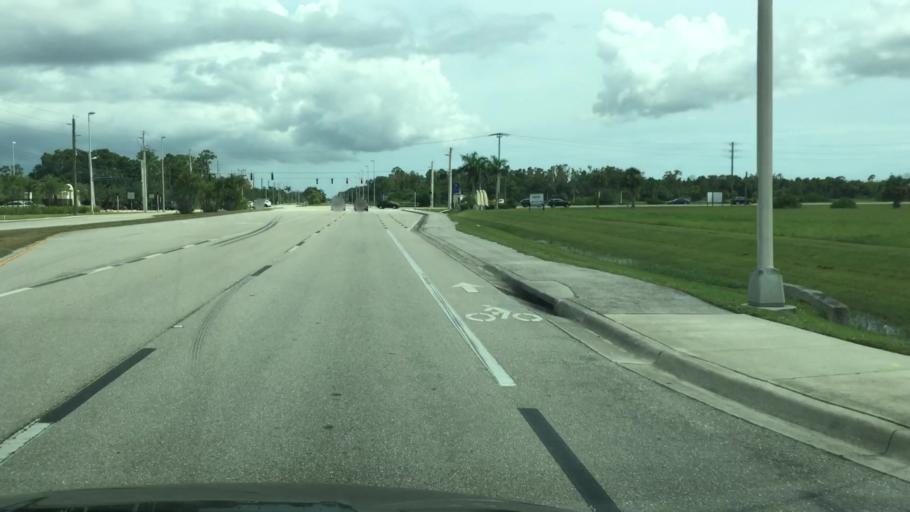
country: US
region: Florida
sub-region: Lee County
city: Three Oaks
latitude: 26.4511
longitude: -81.7890
